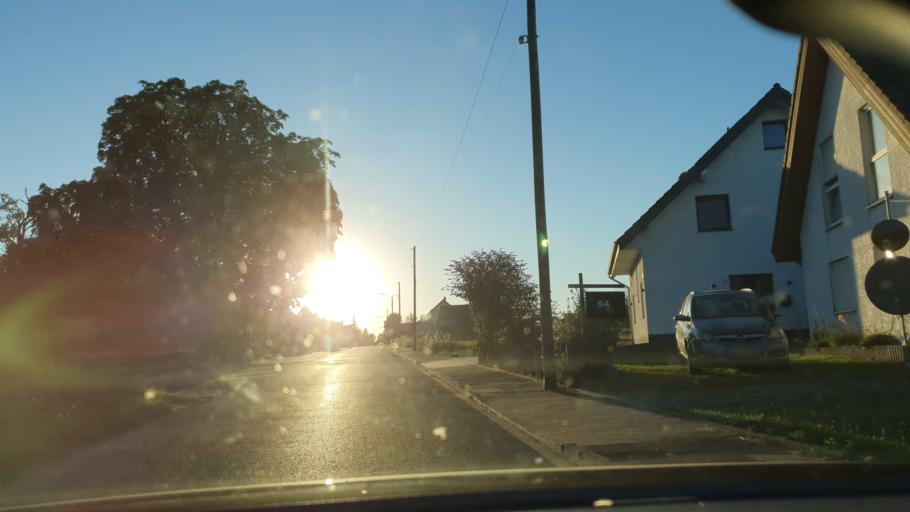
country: DE
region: North Rhine-Westphalia
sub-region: Regierungsbezirk Detmold
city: Rodinghausen
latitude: 52.2096
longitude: 8.5083
